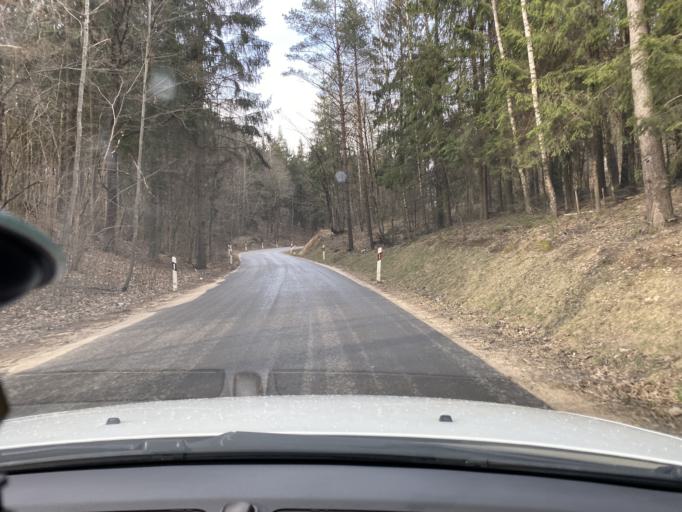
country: LT
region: Vilnius County
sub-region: Vilnius
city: Fabijoniskes
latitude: 54.7597
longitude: 25.2550
